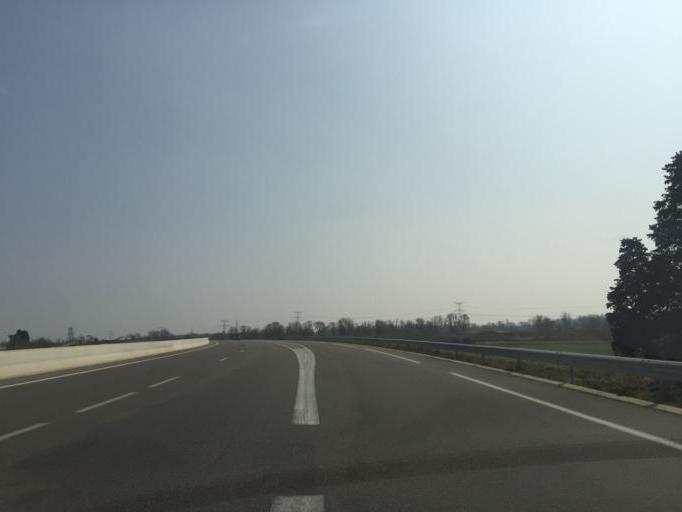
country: FR
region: Provence-Alpes-Cote d'Azur
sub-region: Departement des Bouches-du-Rhone
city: Barbentane
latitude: 43.9241
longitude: 4.7724
